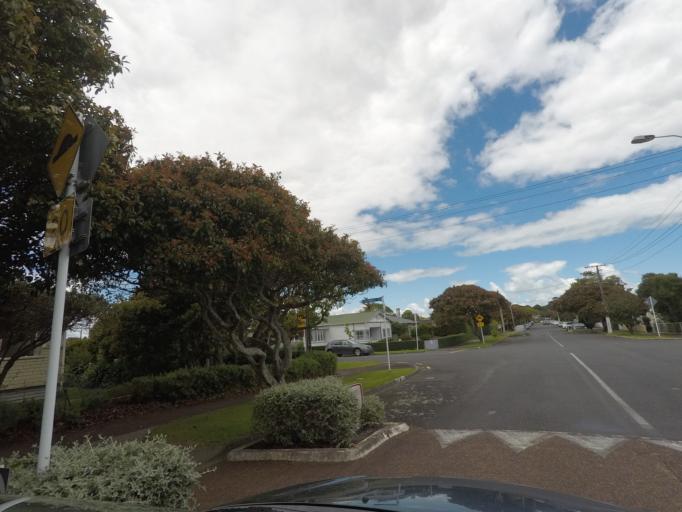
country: NZ
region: Auckland
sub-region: Auckland
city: Auckland
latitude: -36.8874
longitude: 174.7344
